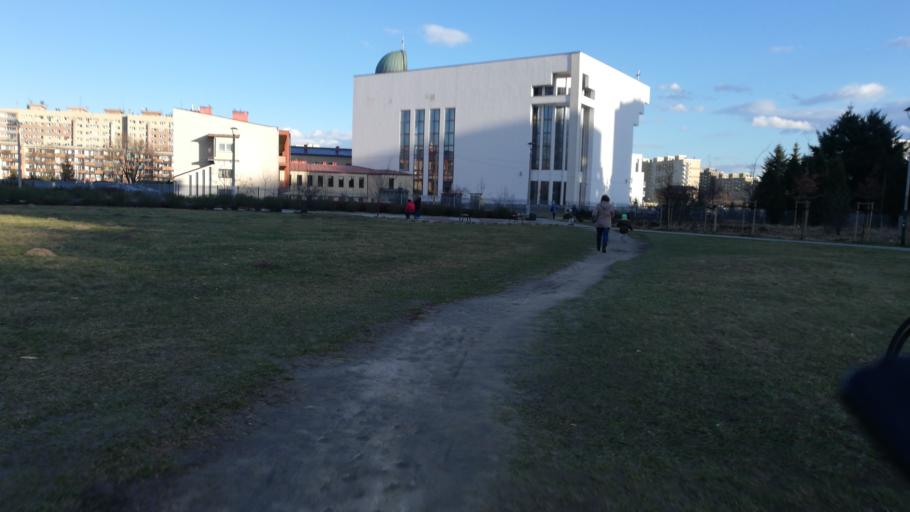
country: PL
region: Lesser Poland Voivodeship
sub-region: Krakow
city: Krakow
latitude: 50.0821
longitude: 20.0063
